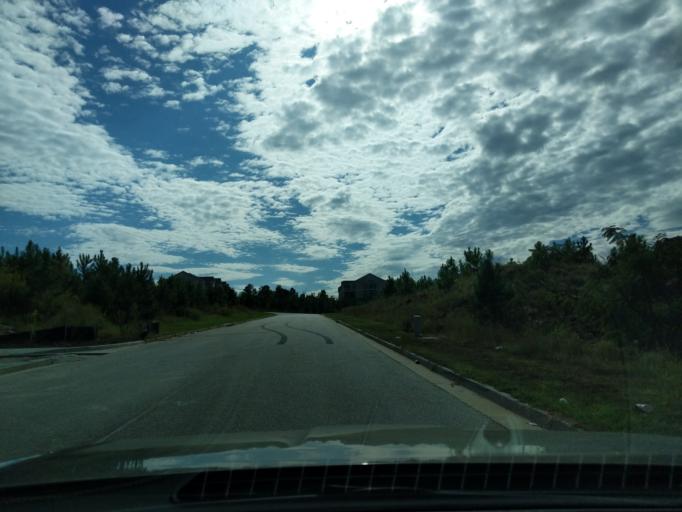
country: US
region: Georgia
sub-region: Columbia County
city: Grovetown
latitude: 33.4811
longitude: -82.2014
